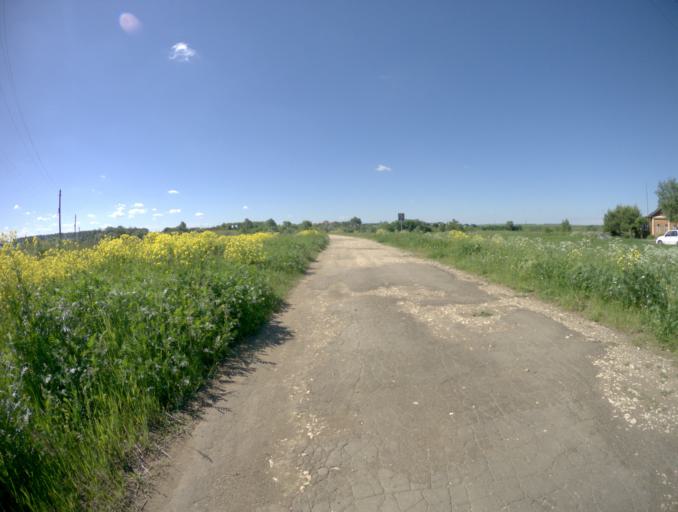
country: RU
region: Ivanovo
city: Gavrilov Posad
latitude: 56.5190
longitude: 40.2131
